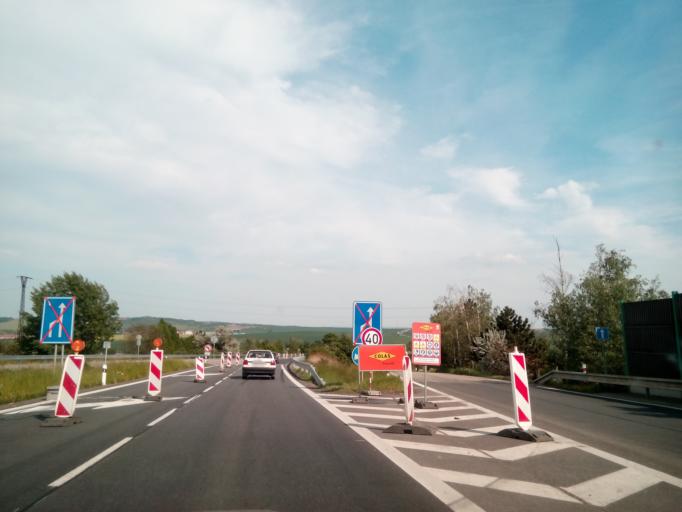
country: CZ
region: South Moravian
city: Blazovice
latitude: 49.1793
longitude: 16.8157
